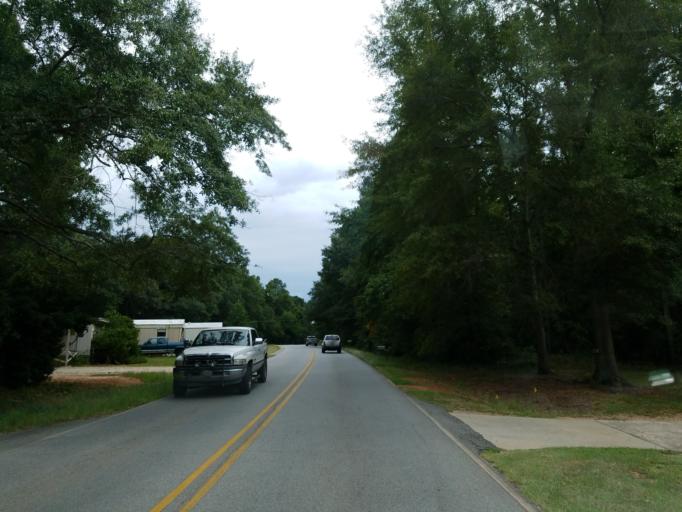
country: US
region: Georgia
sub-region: Spalding County
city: Experiment
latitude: 33.3006
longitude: -84.2877
